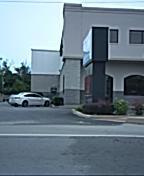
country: US
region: Kentucky
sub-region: Jefferson County
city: Middletown
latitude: 38.2484
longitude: -85.5304
